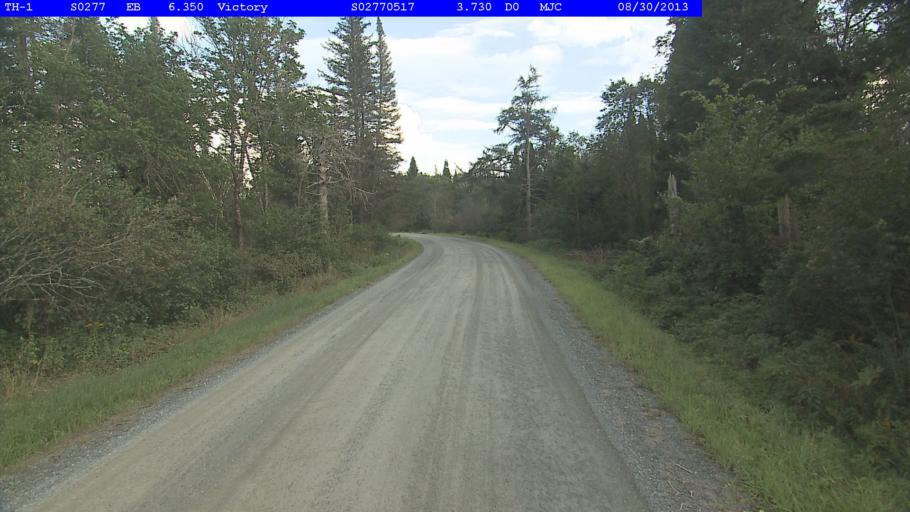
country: US
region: Vermont
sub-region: Caledonia County
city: Lyndonville
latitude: 44.5305
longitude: -71.8041
